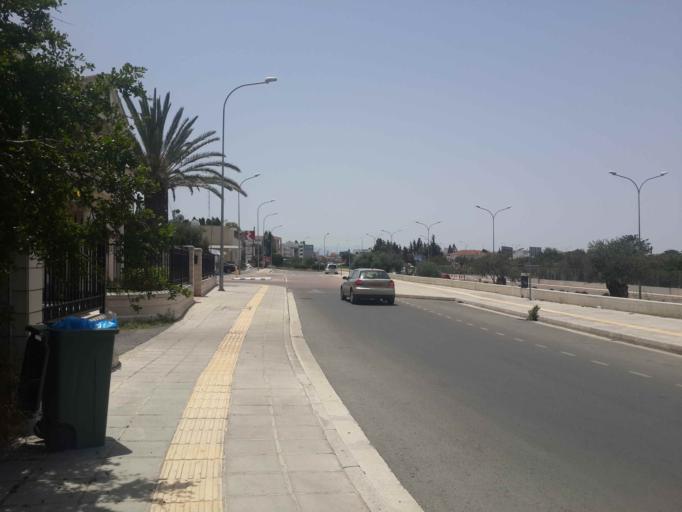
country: CY
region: Lefkosia
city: Nicosia
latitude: 35.1575
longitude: 33.3367
